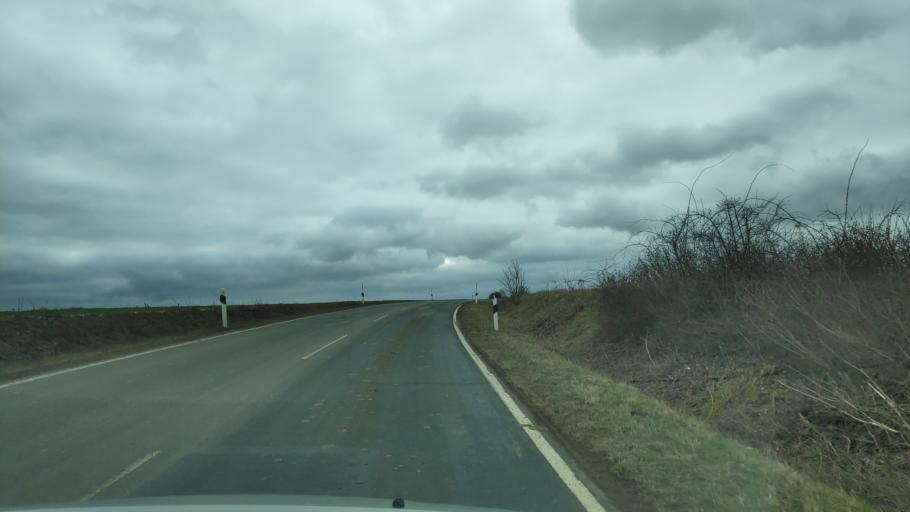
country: DE
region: Lower Saxony
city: Rehren
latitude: 52.2200
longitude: 9.2885
